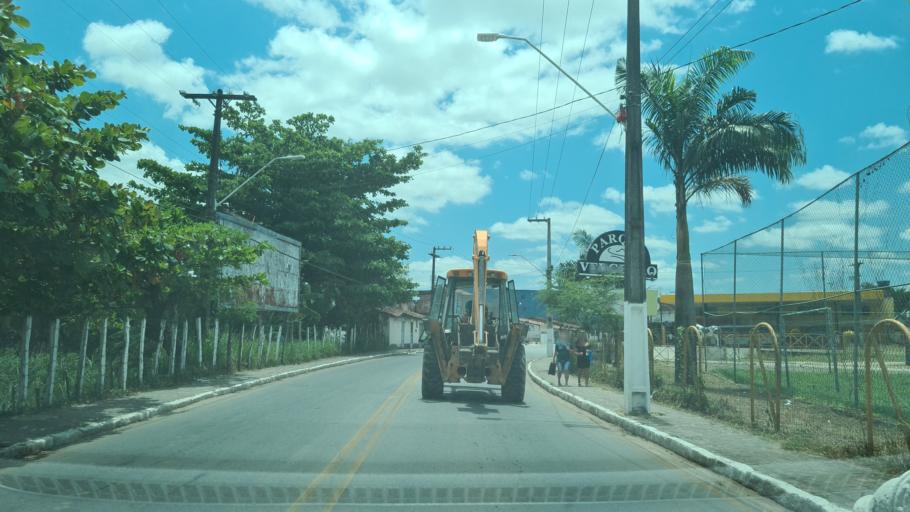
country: BR
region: Alagoas
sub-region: Uniao Dos Palmares
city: Uniao dos Palmares
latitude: -9.1645
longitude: -36.0269
